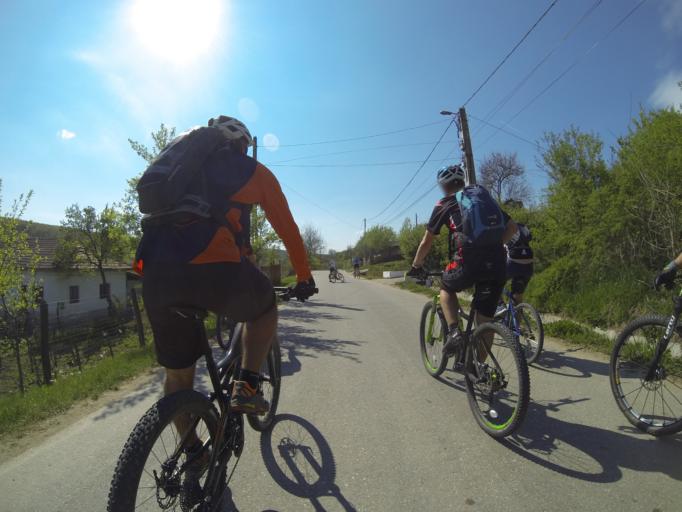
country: RO
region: Gorj
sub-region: Comuna Crusetu
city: Crusetu
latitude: 44.6182
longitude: 23.6632
